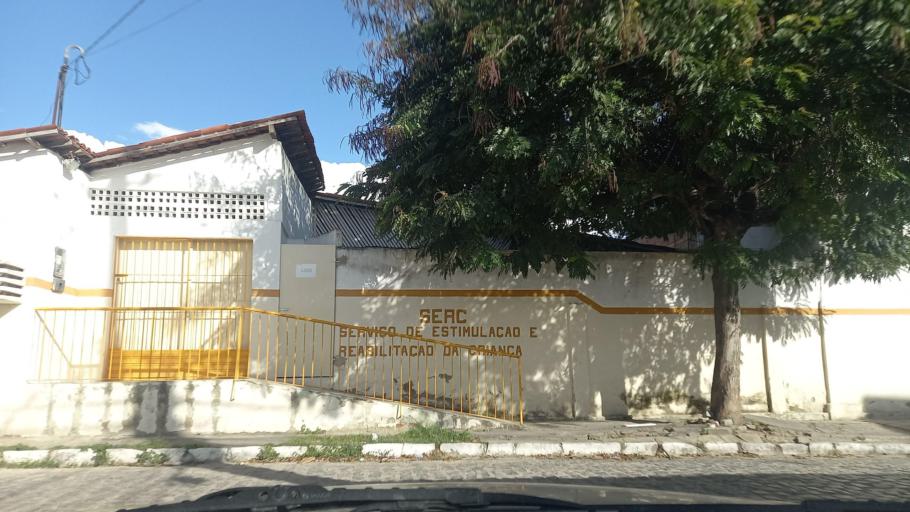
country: BR
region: Pernambuco
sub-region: Gravata
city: Gravata
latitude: -8.2029
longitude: -35.5734
